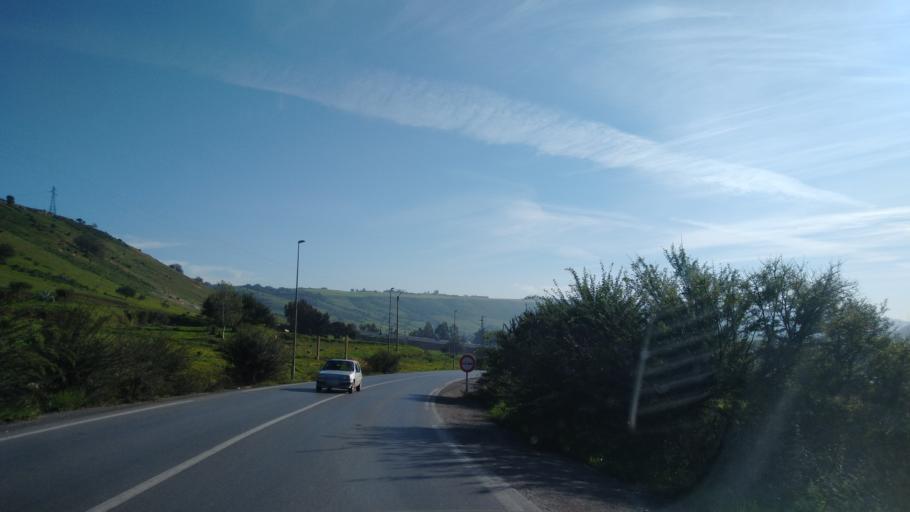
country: MA
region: Rabat-Sale-Zemmour-Zaer
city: Sale
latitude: 33.9905
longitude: -6.7617
